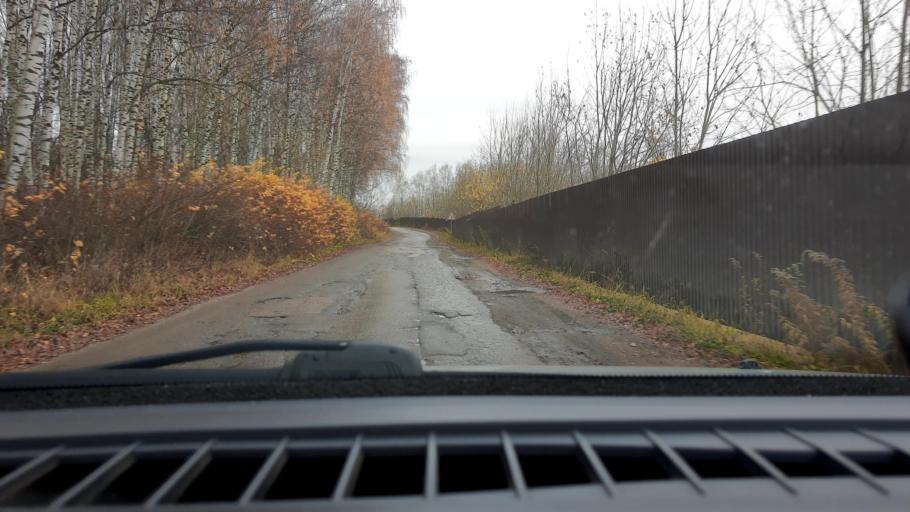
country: RU
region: Nizjnij Novgorod
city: Afonino
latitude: 56.1912
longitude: 44.1090
